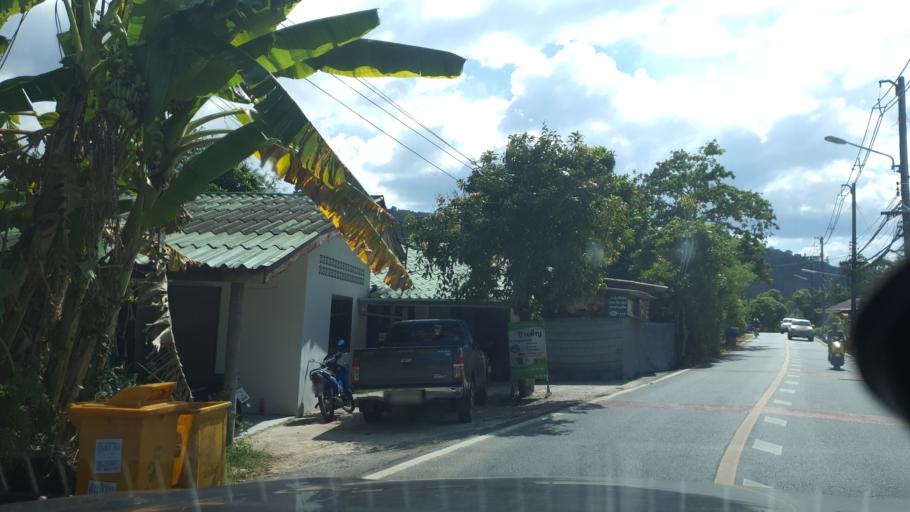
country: TH
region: Phuket
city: Thalang
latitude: 8.0733
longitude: 98.2975
